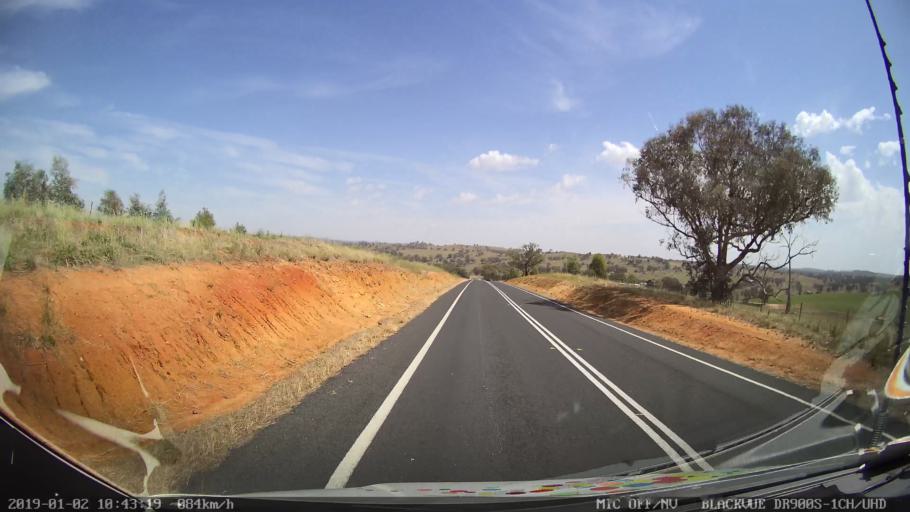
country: AU
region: New South Wales
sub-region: Cootamundra
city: Cootamundra
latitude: -34.7740
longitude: 148.3048
